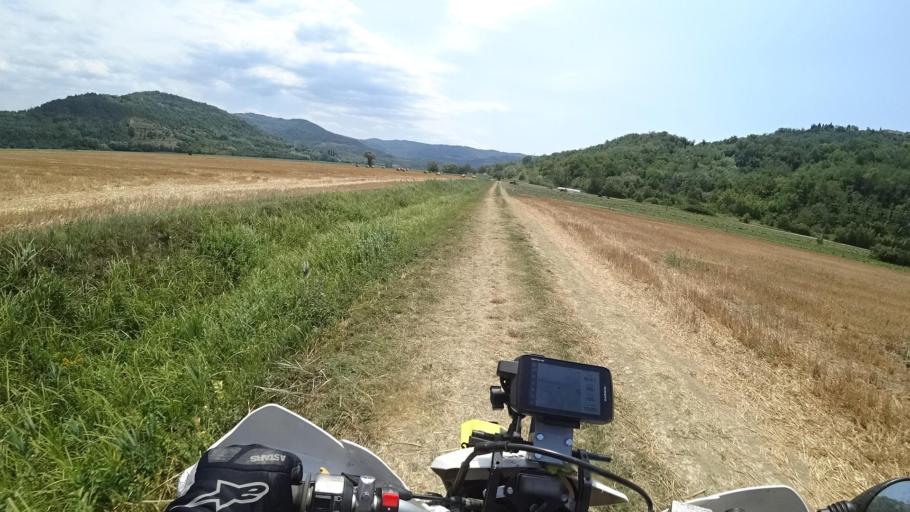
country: HR
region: Istarska
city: Karojba
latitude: 45.3456
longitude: 13.8384
